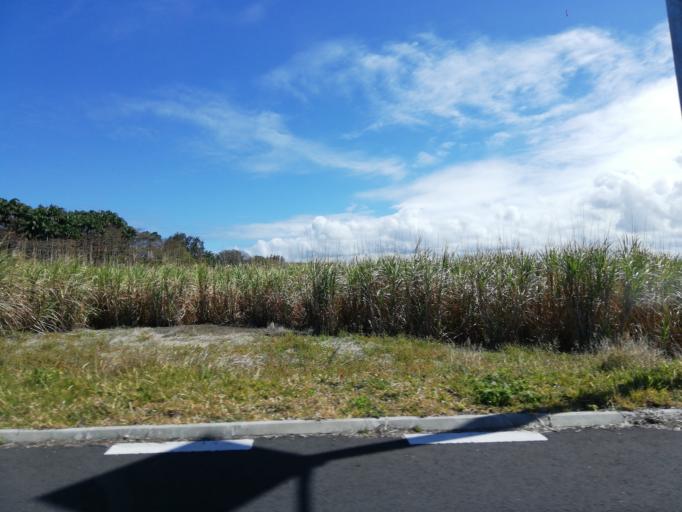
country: MU
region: Grand Port
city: Plaine Magnien
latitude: -20.4517
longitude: 57.6939
